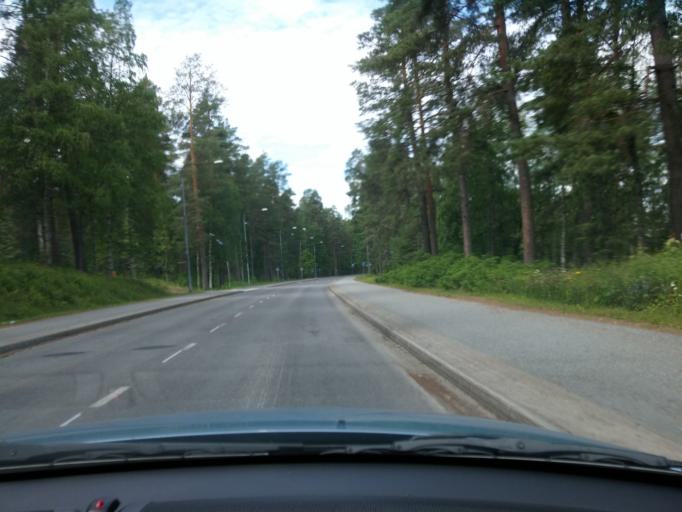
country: FI
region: Central Finland
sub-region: Saarijaervi-Viitasaari
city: Saarijaervi
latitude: 62.7054
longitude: 25.2385
